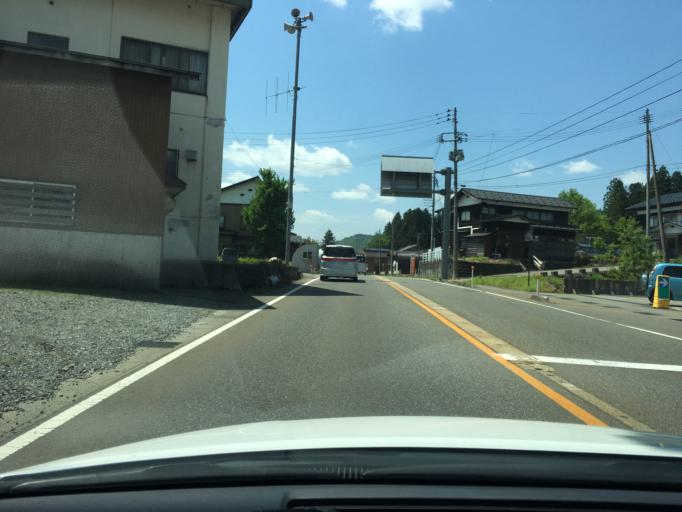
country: JP
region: Niigata
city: Ojiya
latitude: 37.2721
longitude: 138.9774
